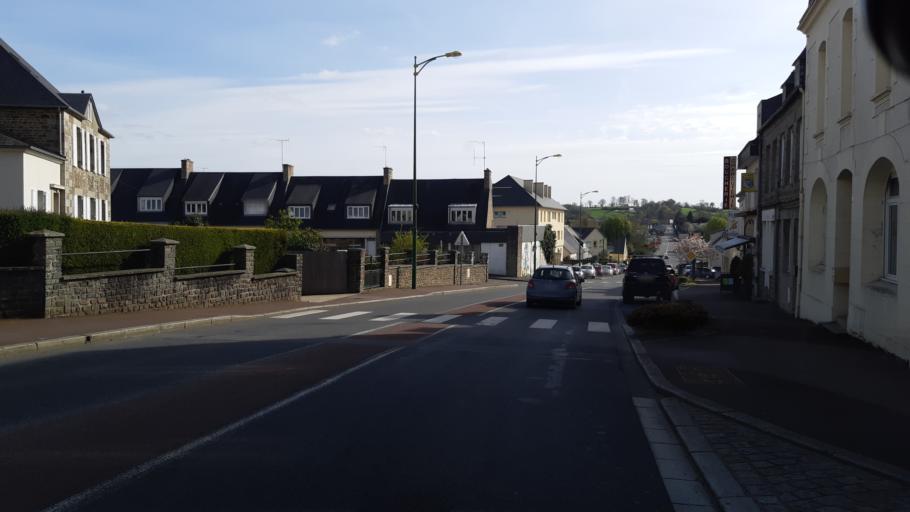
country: FR
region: Lower Normandy
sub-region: Departement de la Manche
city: Percy
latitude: 48.9162
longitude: -1.1914
